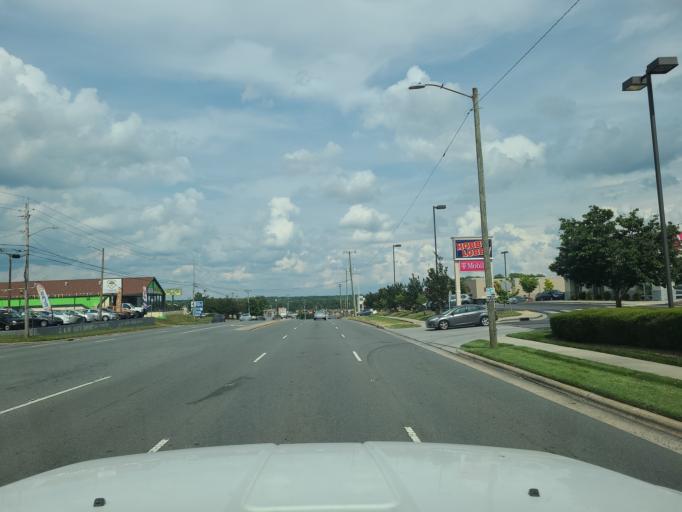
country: US
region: North Carolina
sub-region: Gaston County
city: Ranlo
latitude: 35.2615
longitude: -81.1424
